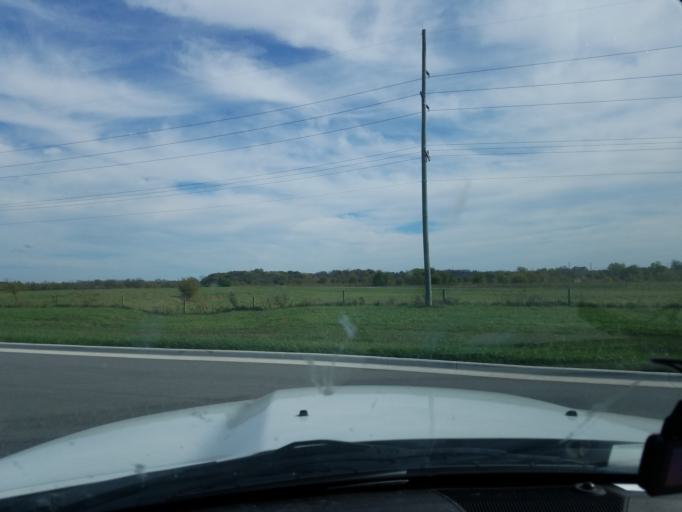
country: US
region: Kentucky
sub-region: Jefferson County
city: Prospect
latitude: 38.3818
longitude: -85.6655
